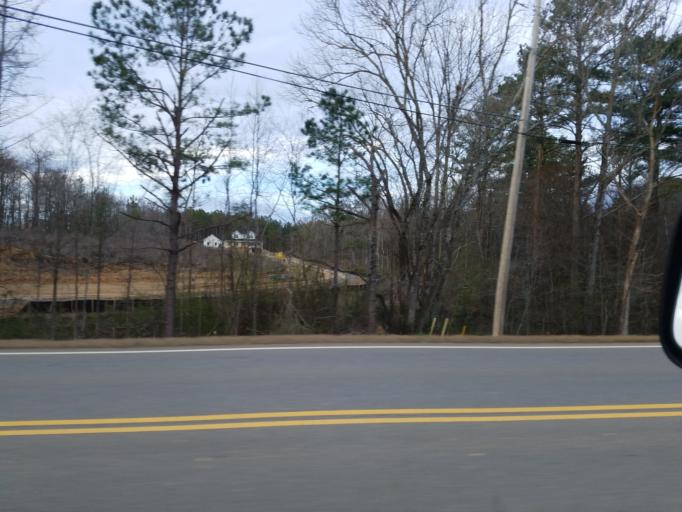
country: US
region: Georgia
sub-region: Bartow County
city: Rydal
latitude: 34.4478
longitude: -84.7783
